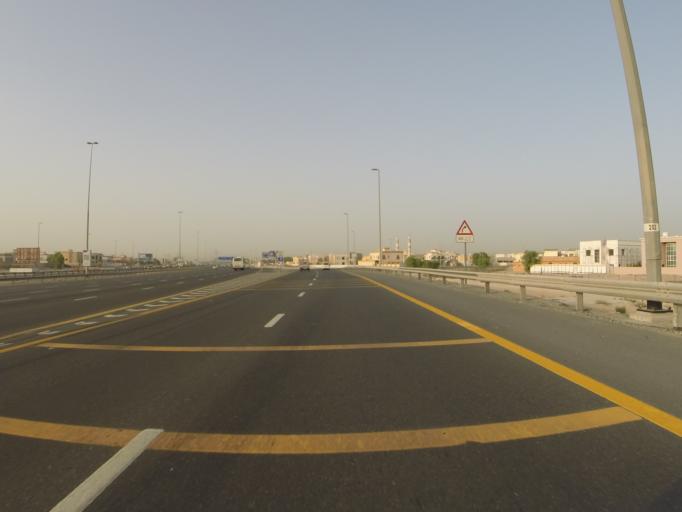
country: AE
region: Dubai
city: Dubai
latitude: 25.1607
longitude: 55.2615
